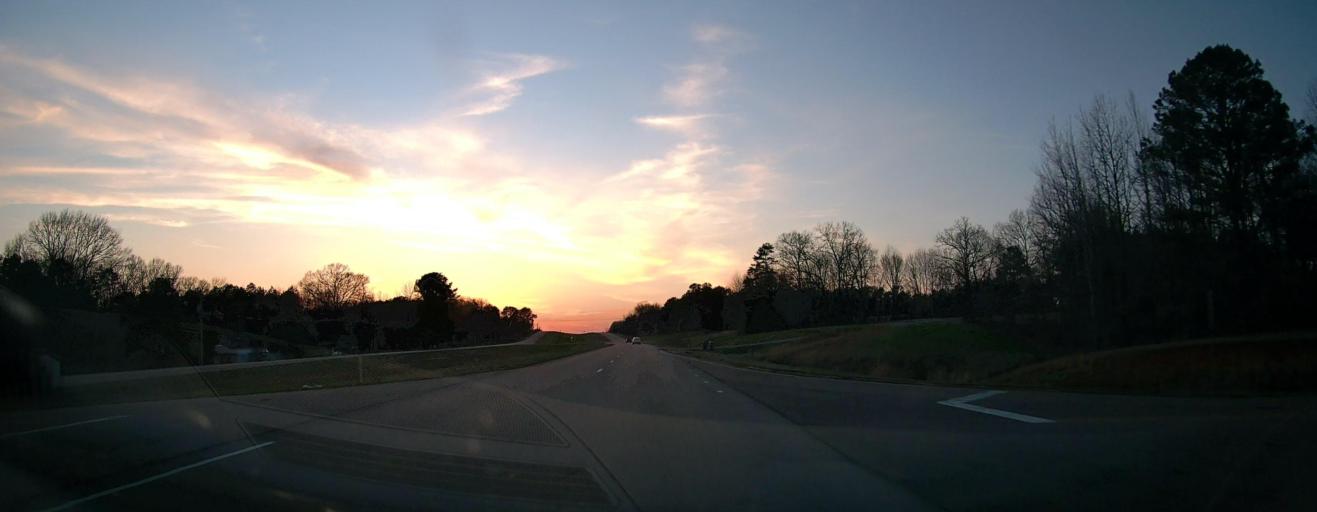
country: US
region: Mississippi
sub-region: Tippah County
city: Ripley
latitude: 34.9525
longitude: -88.8325
